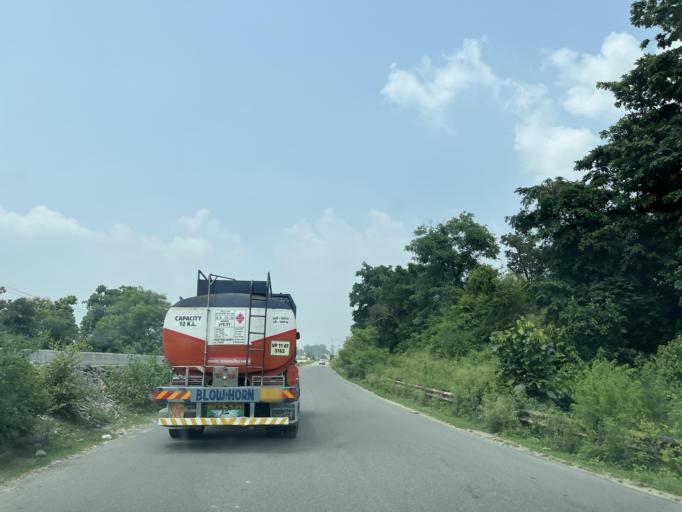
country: IN
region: Uttarakhand
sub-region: Haridwar
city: Haridwar
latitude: 29.8573
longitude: 78.1863
